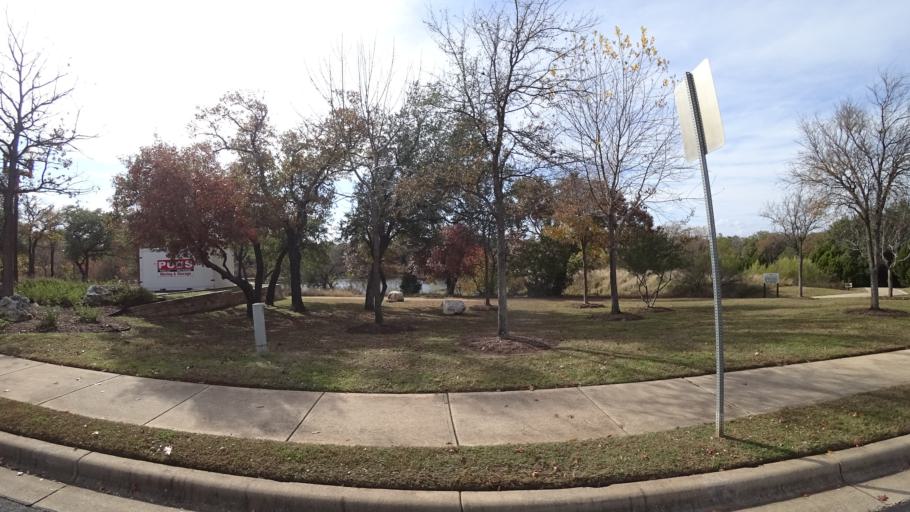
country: US
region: Texas
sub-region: Williamson County
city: Brushy Creek
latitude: 30.5113
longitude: -97.7489
